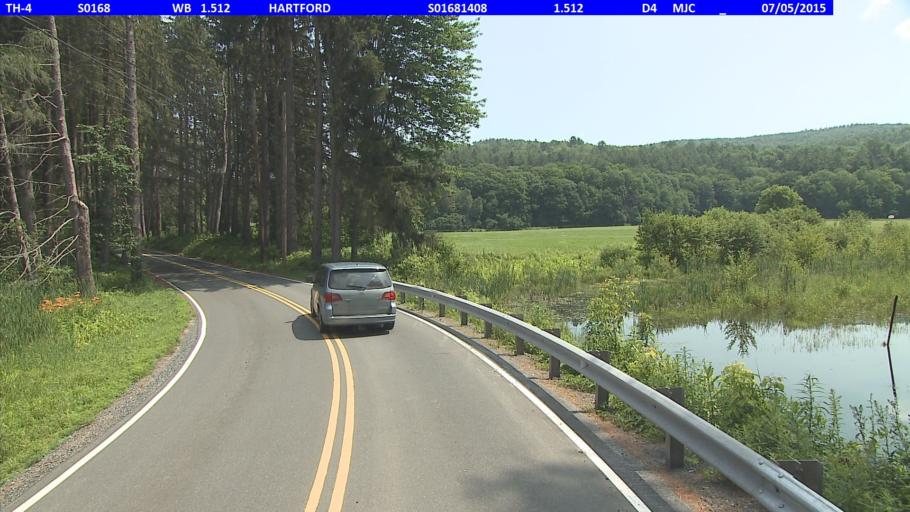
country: US
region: Vermont
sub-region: Windsor County
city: White River Junction
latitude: 43.6418
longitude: -72.4007
